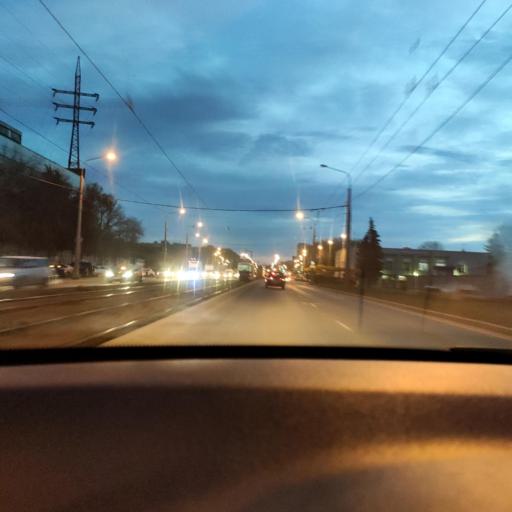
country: RU
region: Samara
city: Samara
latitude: 53.2047
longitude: 50.2709
